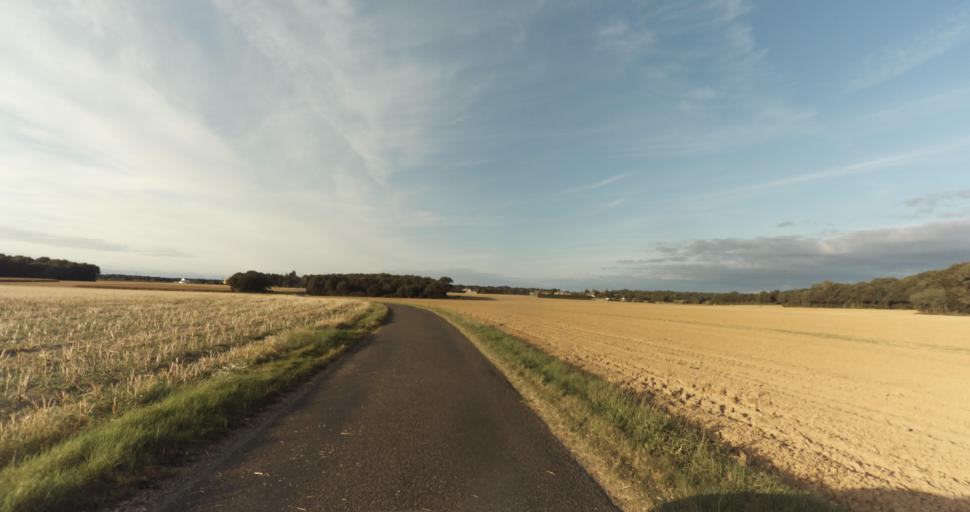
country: FR
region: Haute-Normandie
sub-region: Departement de l'Eure
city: Saint-Germain-sur-Avre
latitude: 48.8321
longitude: 1.2774
